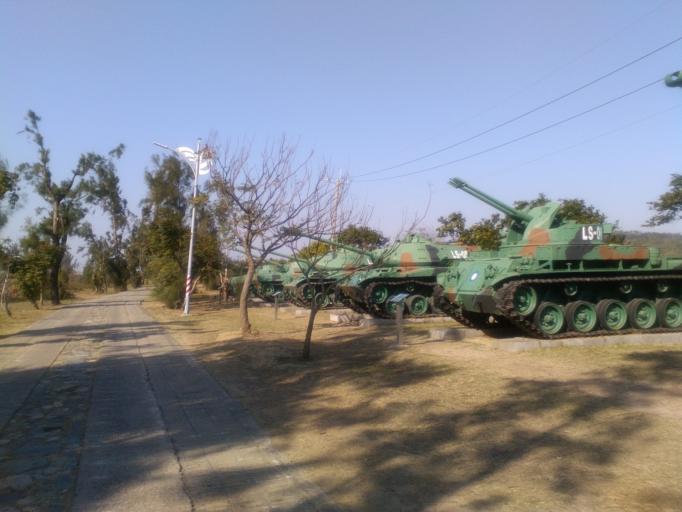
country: TW
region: Fukien
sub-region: Kinmen
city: Jincheng
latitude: 24.4357
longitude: 118.2292
